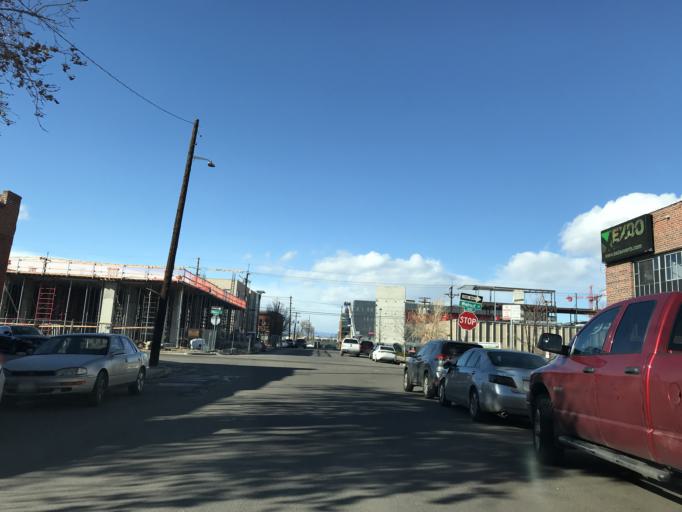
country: US
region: Colorado
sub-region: Denver County
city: Denver
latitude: 39.7674
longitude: -104.9750
